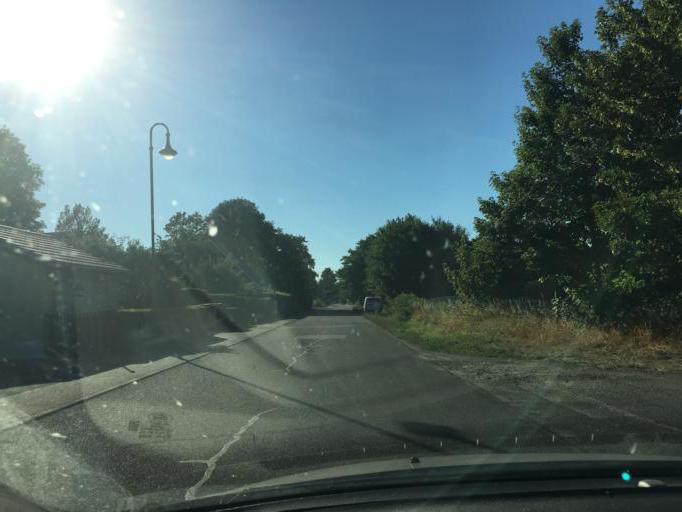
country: DE
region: Saxony
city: Grossposna
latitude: 51.2787
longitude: 12.4747
